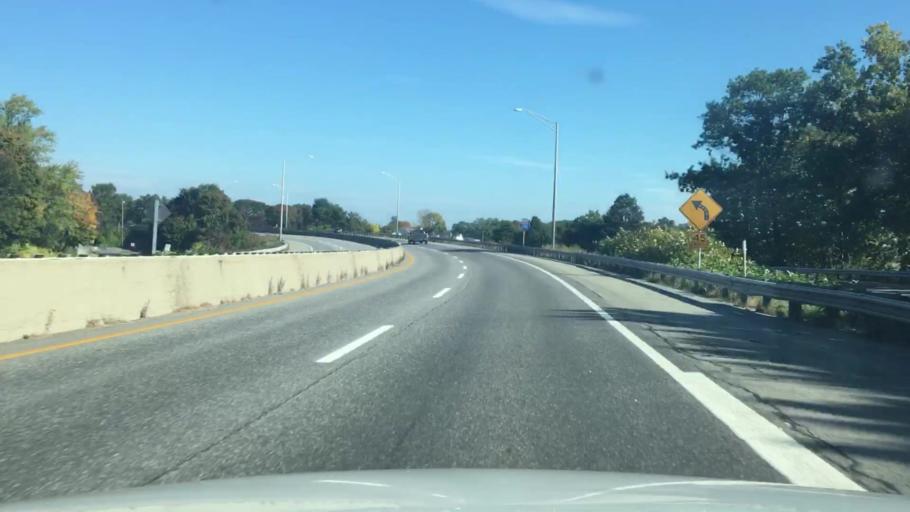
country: US
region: Maine
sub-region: Cumberland County
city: Portland
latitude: 43.6833
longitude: -70.2527
